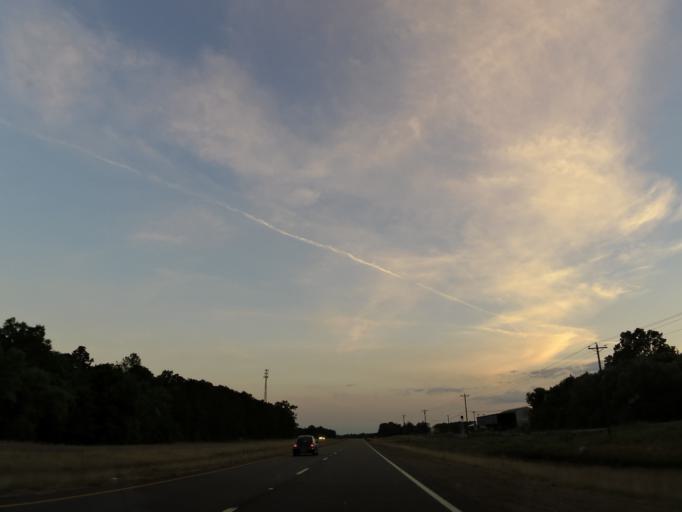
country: US
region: Mississippi
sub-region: Kemper County
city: De Kalb
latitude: 32.7745
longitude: -88.4621
